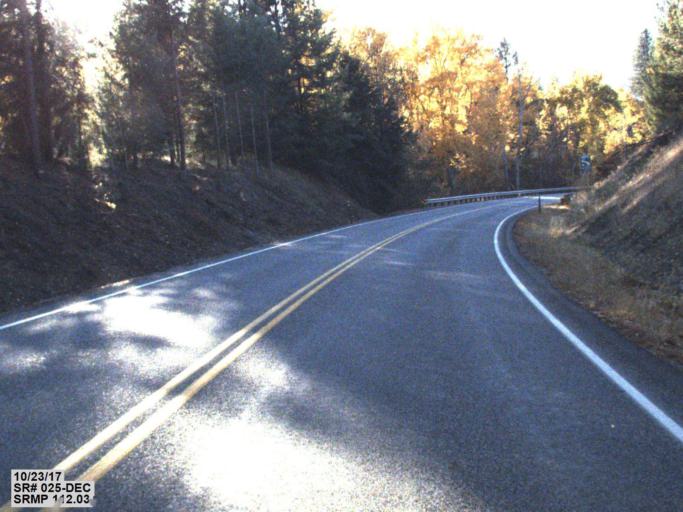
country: CA
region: British Columbia
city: Rossland
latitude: 48.8991
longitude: -117.7979
